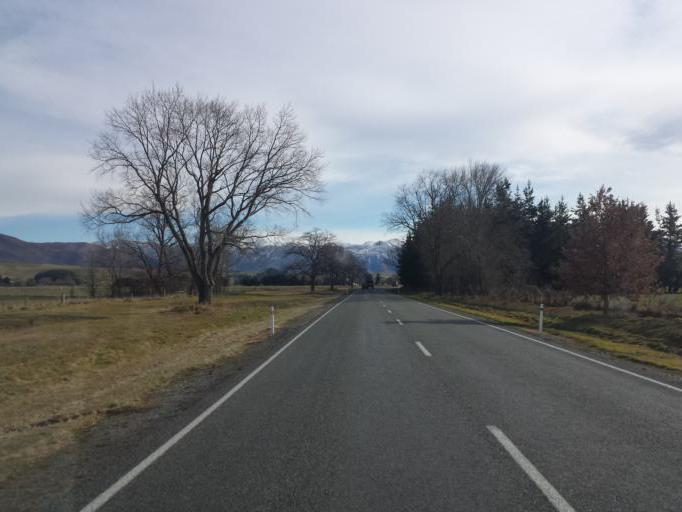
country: NZ
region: Canterbury
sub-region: Timaru District
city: Pleasant Point
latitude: -44.0802
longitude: 170.8049
